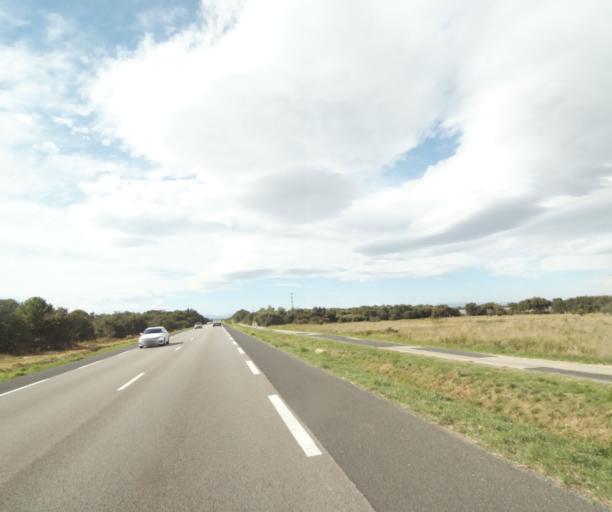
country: FR
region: Languedoc-Roussillon
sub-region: Departement des Pyrenees-Orientales
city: Sant Andreu de Sureda
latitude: 42.5540
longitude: 2.9901
